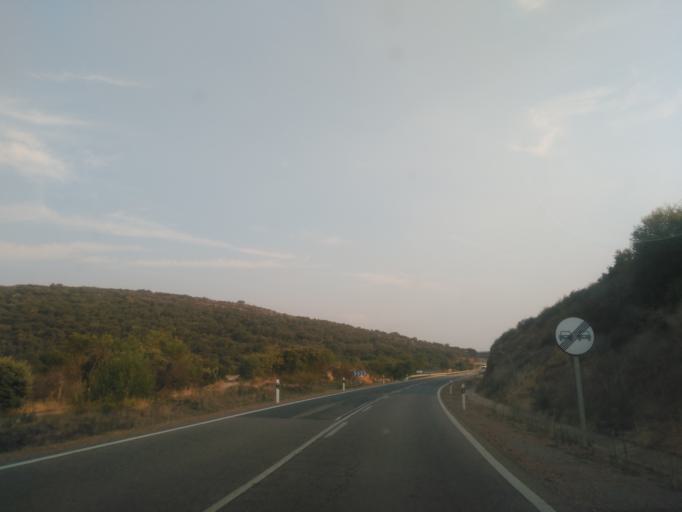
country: ES
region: Castille and Leon
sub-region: Provincia de Zamora
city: Perilla de Castro
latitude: 41.7547
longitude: -5.8549
